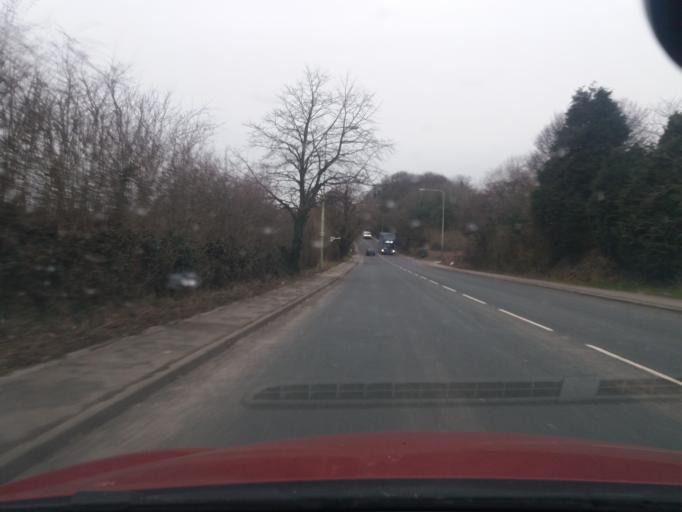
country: GB
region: England
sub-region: Lancashire
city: Chorley
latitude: 53.6736
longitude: -2.6160
